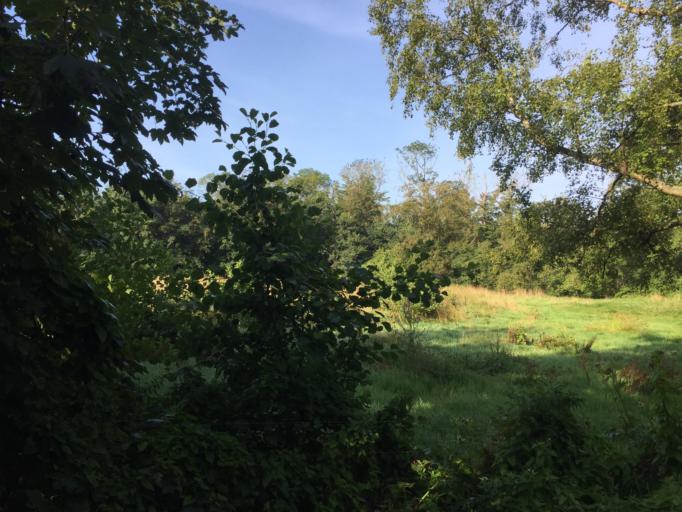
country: DK
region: South Denmark
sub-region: Odense Kommune
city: Neder Holluf
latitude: 55.3537
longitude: 10.4423
